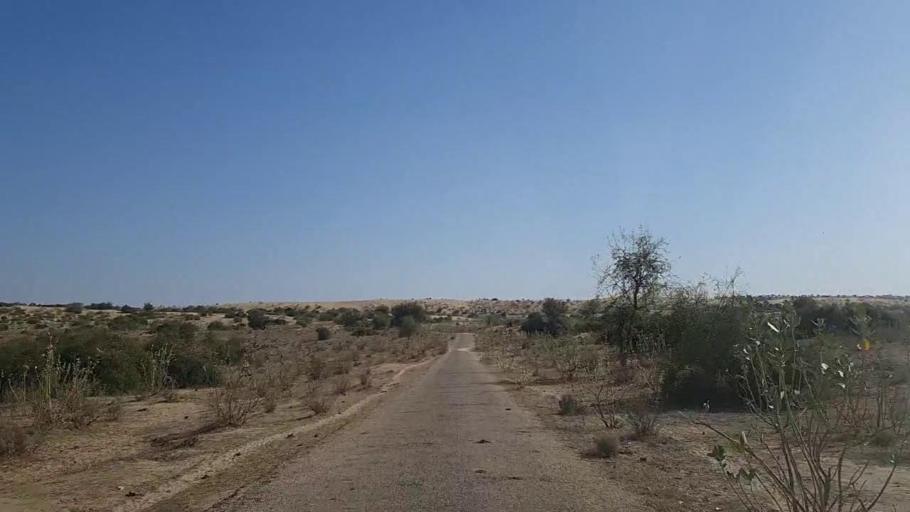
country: PK
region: Sindh
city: Naukot
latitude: 24.8388
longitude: 69.5533
